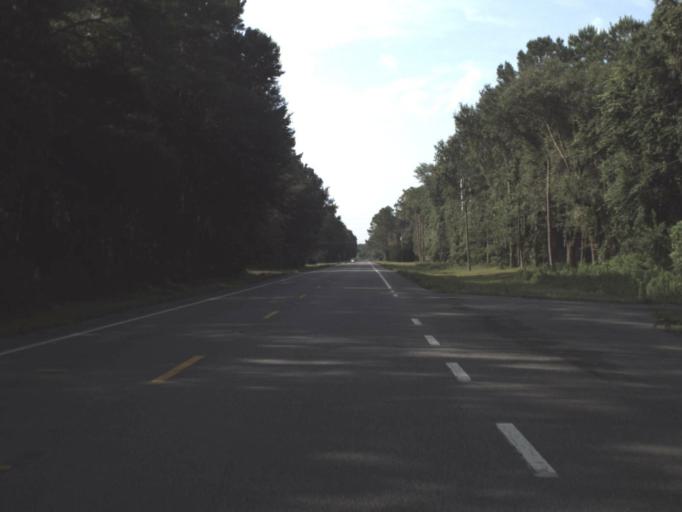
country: US
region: Florida
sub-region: Taylor County
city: Perry
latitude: 30.1744
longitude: -83.5983
